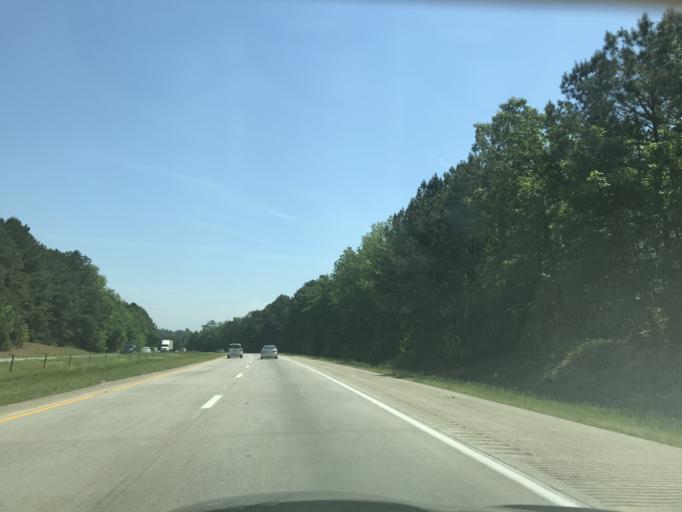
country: US
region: North Carolina
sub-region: Johnston County
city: Benson
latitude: 35.4698
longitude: -78.5485
